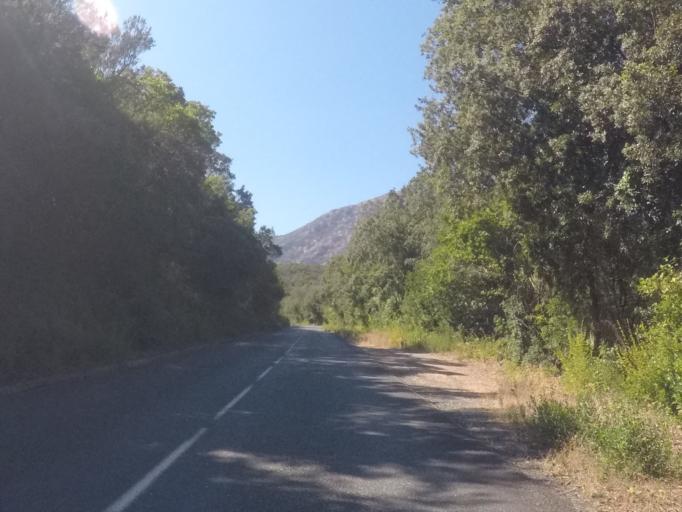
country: FR
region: Corsica
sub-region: Departement de la Haute-Corse
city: Calvi
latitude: 42.3842
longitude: 8.6915
